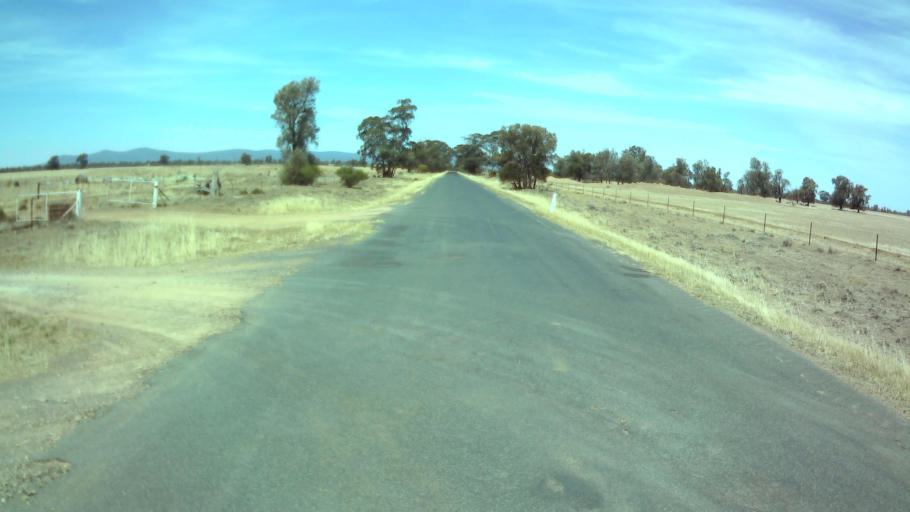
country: AU
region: New South Wales
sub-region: Weddin
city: Grenfell
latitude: -33.9408
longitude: 147.7673
